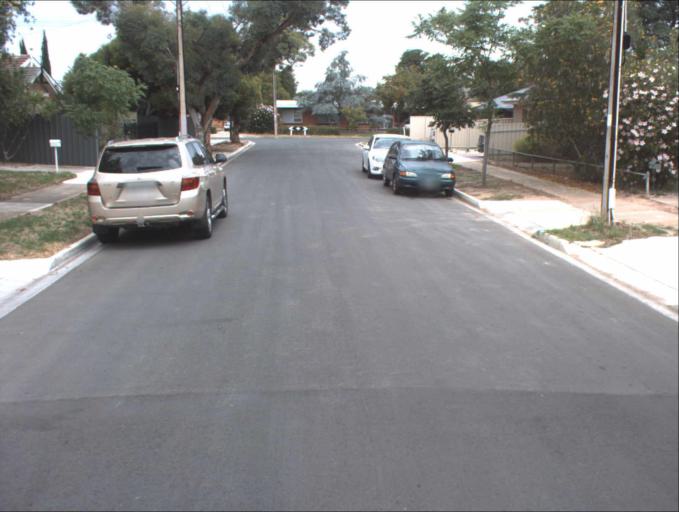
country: AU
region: South Australia
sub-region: Port Adelaide Enfield
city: Enfield
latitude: -34.8510
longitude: 138.6216
